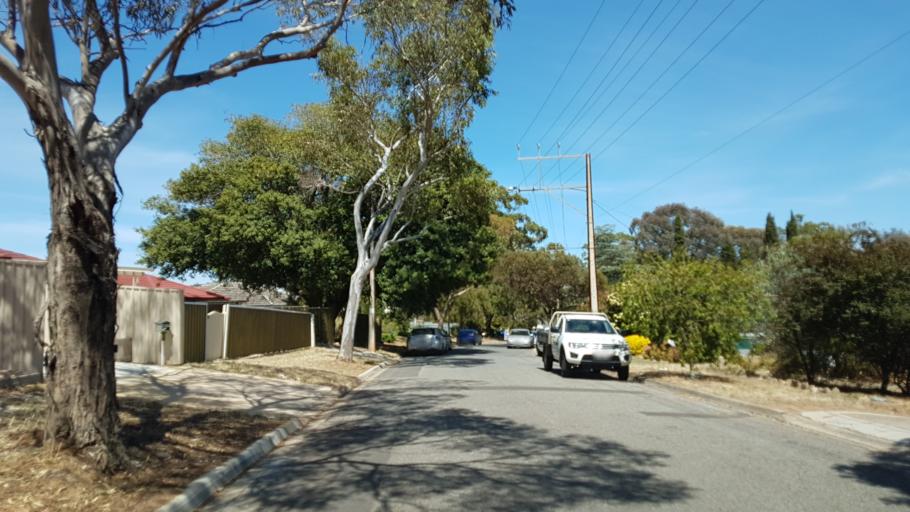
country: AU
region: South Australia
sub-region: Tea Tree Gully
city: Hope Valley
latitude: -34.8226
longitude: 138.7170
